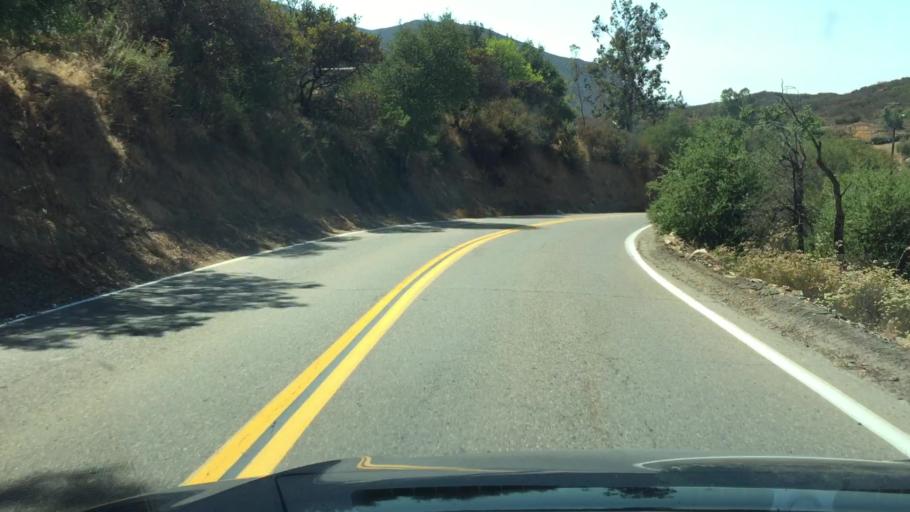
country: US
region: California
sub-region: San Diego County
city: Alpine
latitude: 32.7537
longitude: -116.7767
